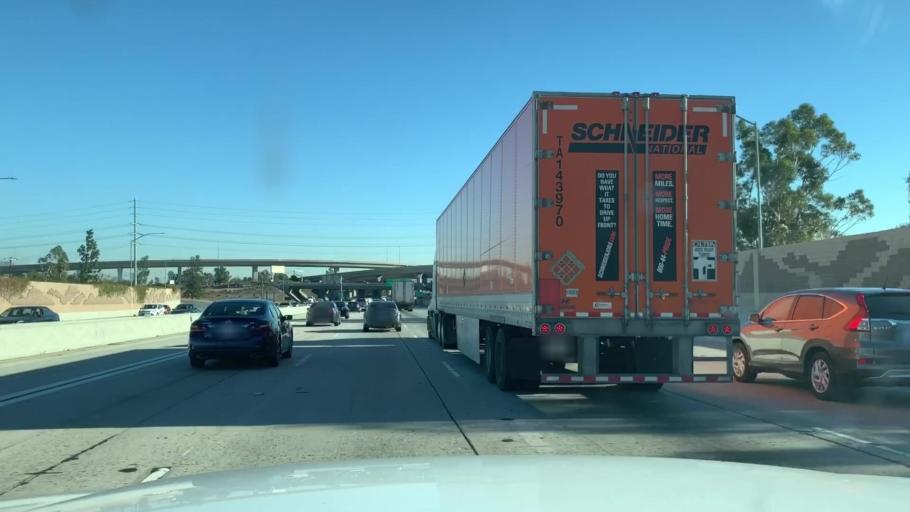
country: US
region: California
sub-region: Los Angeles County
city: San Fernando
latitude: 34.2692
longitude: -118.4462
